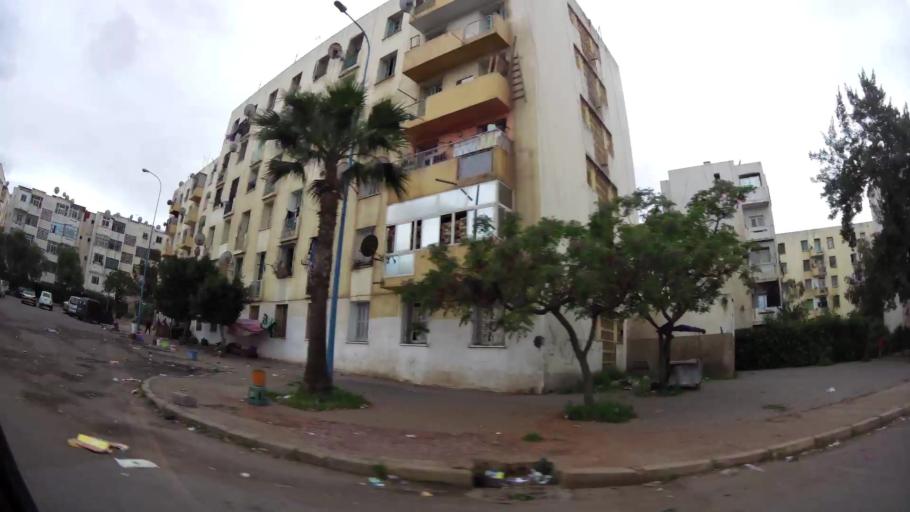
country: MA
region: Grand Casablanca
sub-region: Casablanca
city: Casablanca
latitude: 33.5747
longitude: -7.5549
